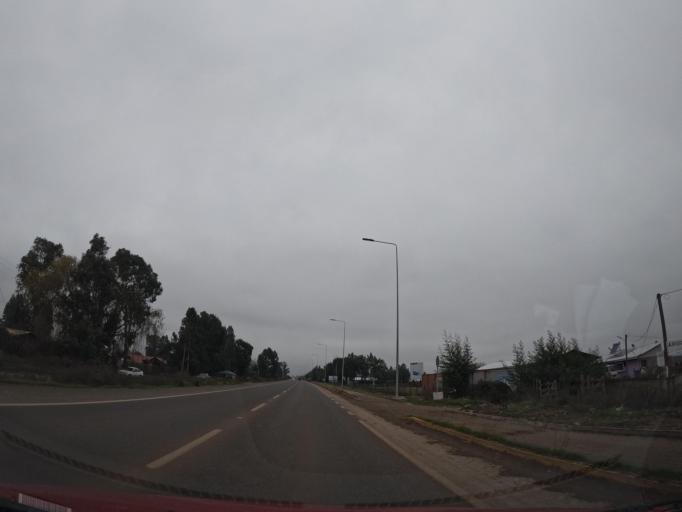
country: CL
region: Maule
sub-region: Provincia de Talca
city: San Clemente
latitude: -35.5225
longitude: -71.4879
